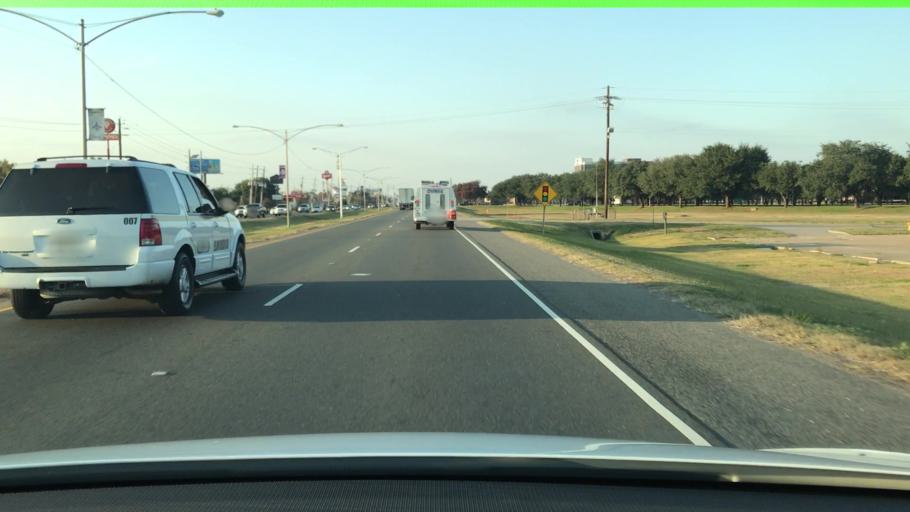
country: US
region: Louisiana
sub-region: Bossier Parish
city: Bossier City
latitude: 32.4243
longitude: -93.7074
